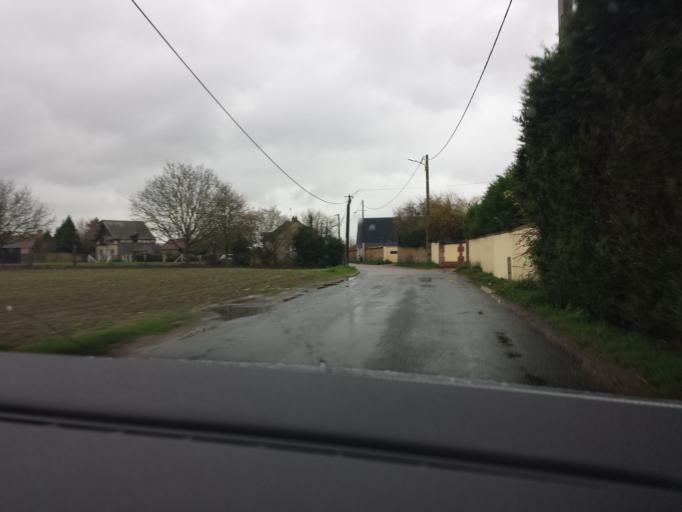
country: FR
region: Haute-Normandie
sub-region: Departement de l'Eure
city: Evreux
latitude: 49.0090
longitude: 1.1927
